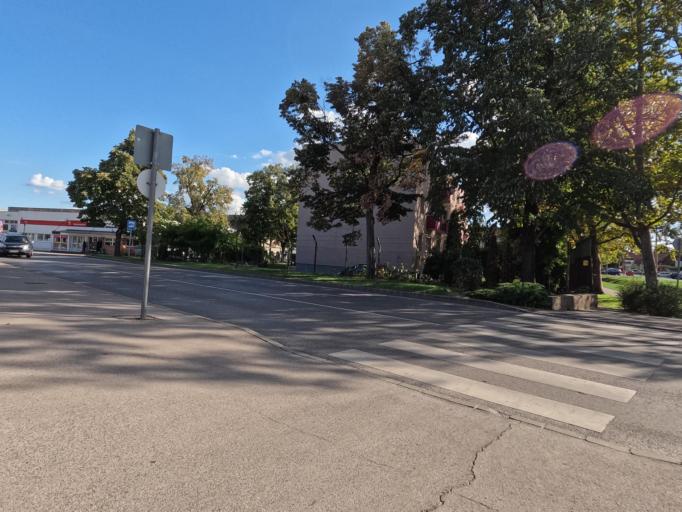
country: HU
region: Tolna
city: Paks
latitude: 46.6202
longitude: 18.8534
